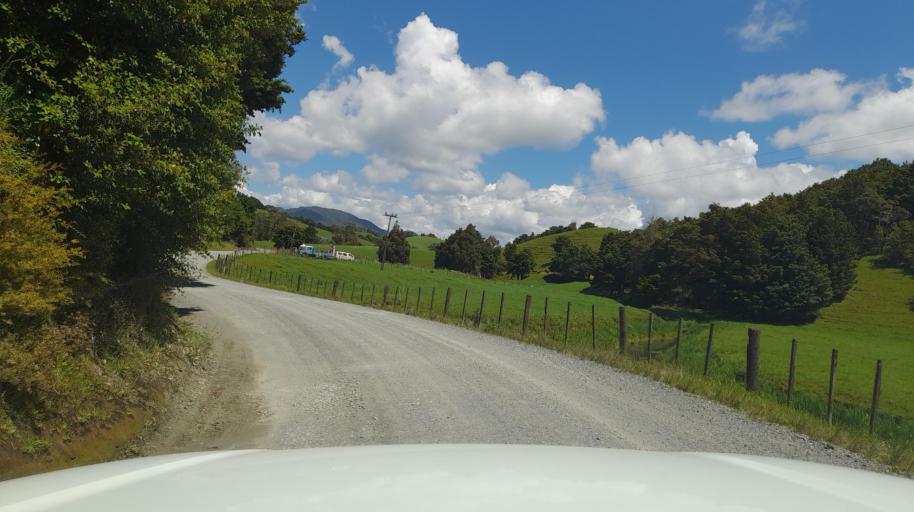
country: NZ
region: Northland
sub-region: Far North District
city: Kaitaia
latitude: -35.1091
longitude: 173.3952
